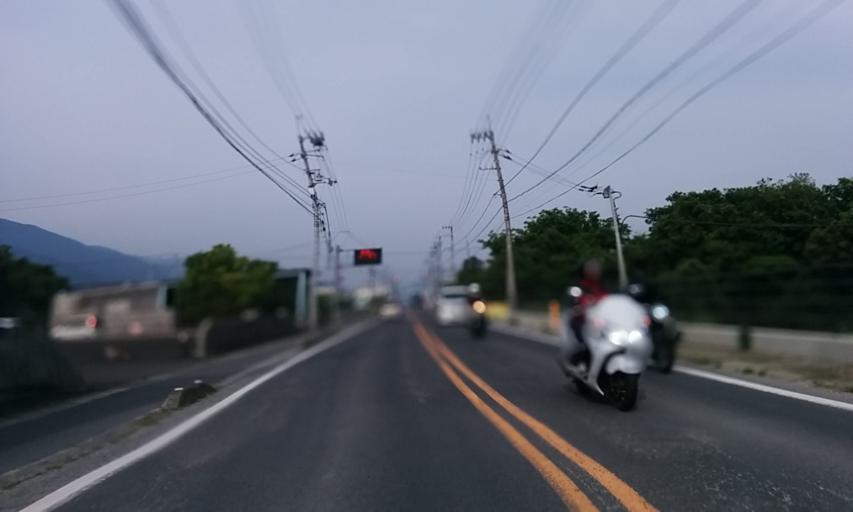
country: JP
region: Ehime
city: Kawanoecho
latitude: 33.9631
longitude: 133.4618
